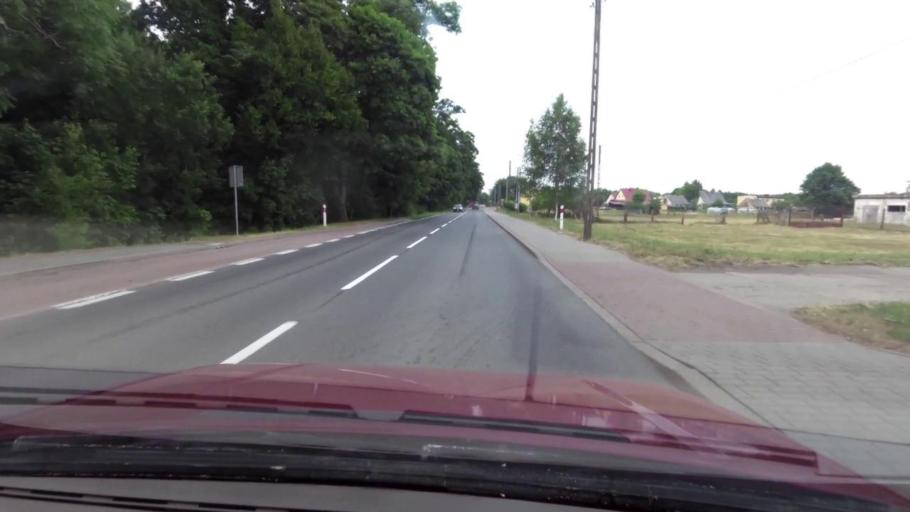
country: PL
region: Pomeranian Voivodeship
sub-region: Powiat bytowski
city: Trzebielino
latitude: 54.2051
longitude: 17.0893
